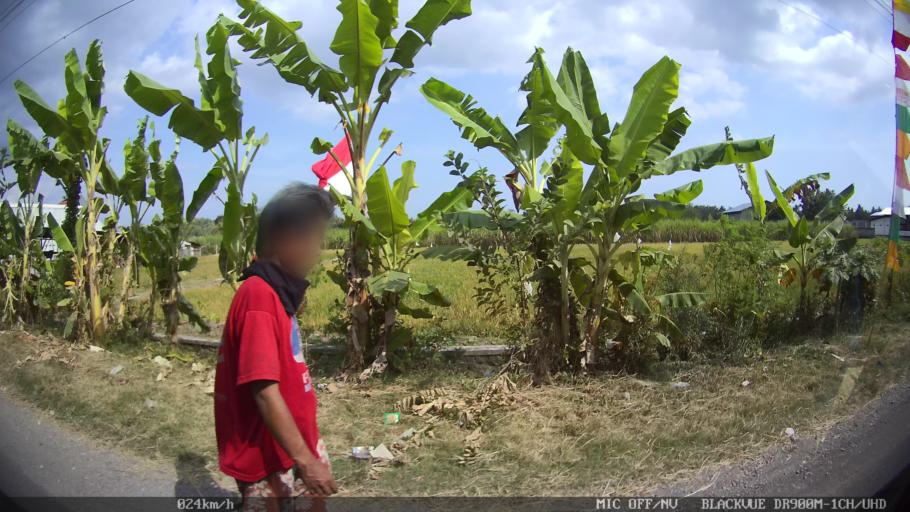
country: ID
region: Daerah Istimewa Yogyakarta
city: Kasihan
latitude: -7.8290
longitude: 110.3210
